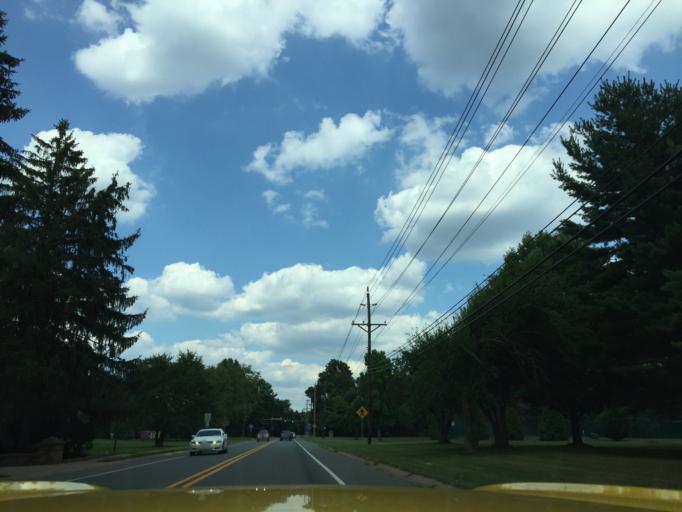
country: US
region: Delaware
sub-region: New Castle County
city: Bellefonte
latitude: 39.8108
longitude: -75.5268
